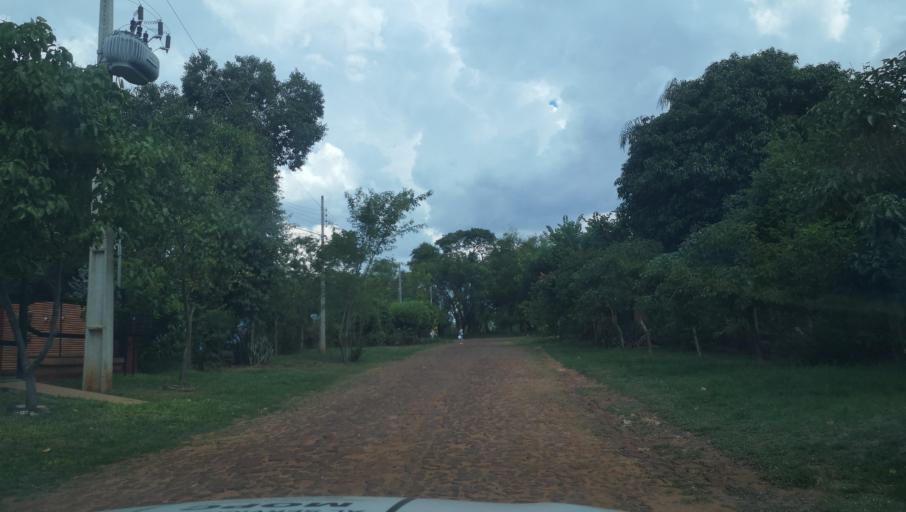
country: PY
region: Misiones
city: Santa Maria
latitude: -26.8882
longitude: -57.0105
